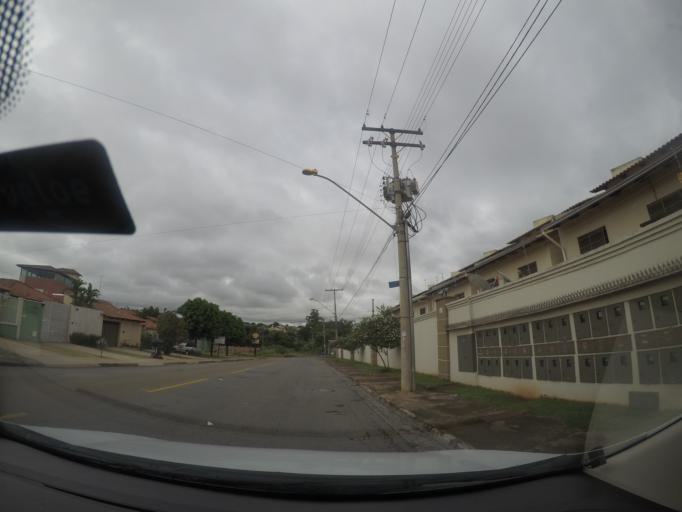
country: BR
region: Goias
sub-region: Goiania
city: Goiania
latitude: -16.7220
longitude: -49.2926
